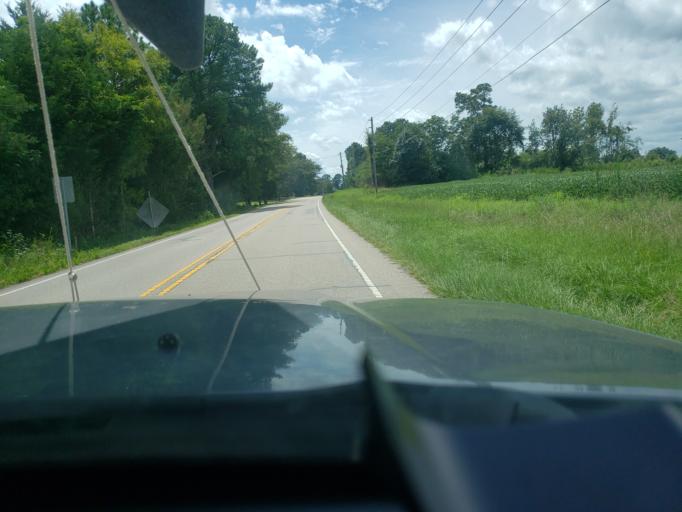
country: US
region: North Carolina
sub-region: Wake County
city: Rolesville
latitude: 35.8851
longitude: -78.4402
